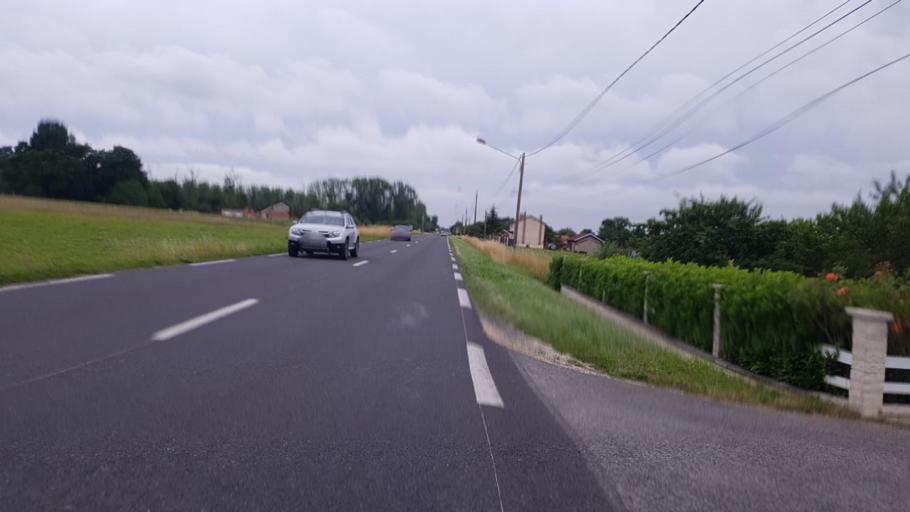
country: FR
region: Champagne-Ardenne
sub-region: Departement de la Marne
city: Pargny-sur-Saulx
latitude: 48.7741
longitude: 4.8684
